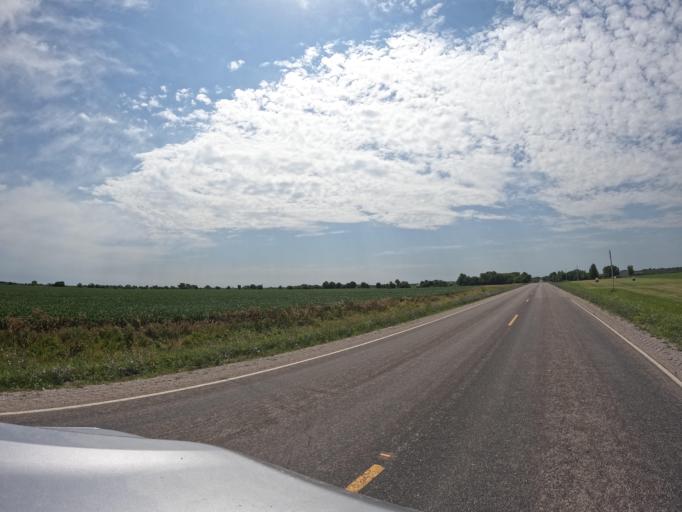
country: US
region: Iowa
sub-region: Appanoose County
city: Centerville
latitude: 40.8079
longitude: -92.9449
